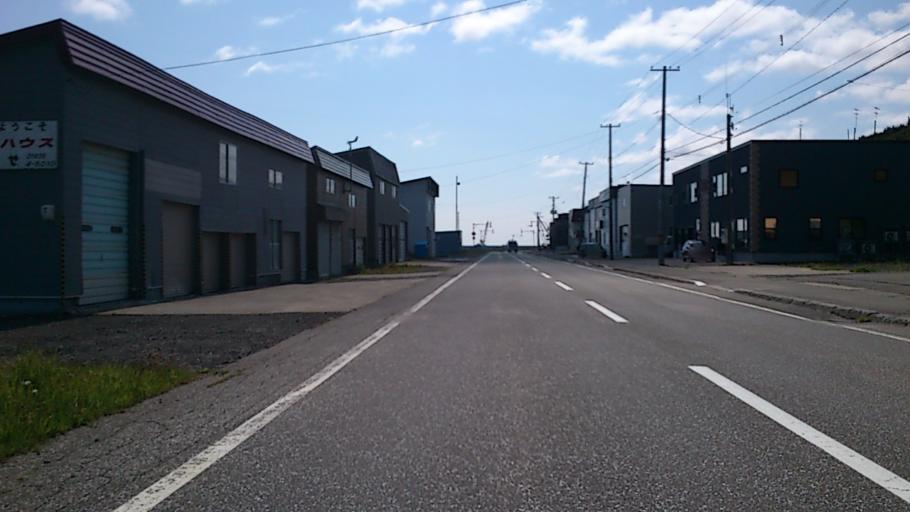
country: JP
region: Hokkaido
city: Makubetsu
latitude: 45.3848
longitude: 142.0805
